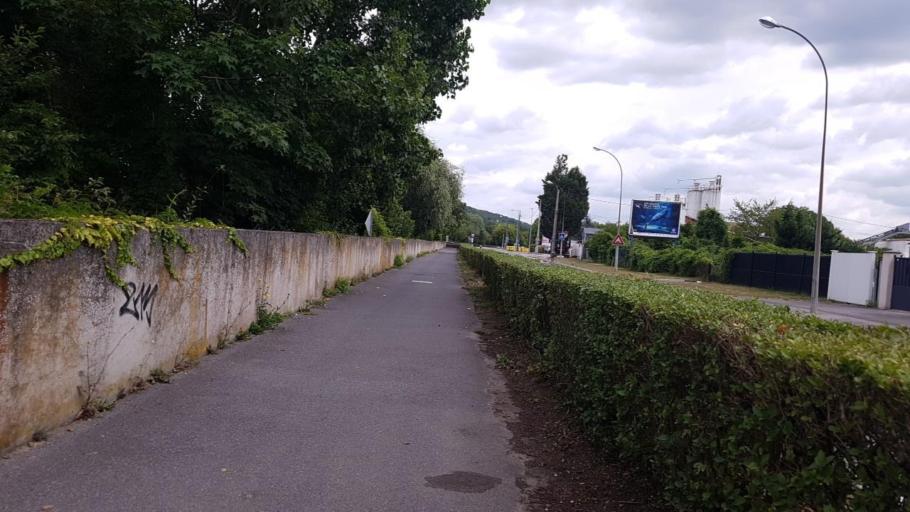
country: FR
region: Picardie
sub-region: Departement de l'Oise
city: Compiegne
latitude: 49.4281
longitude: 2.8368
